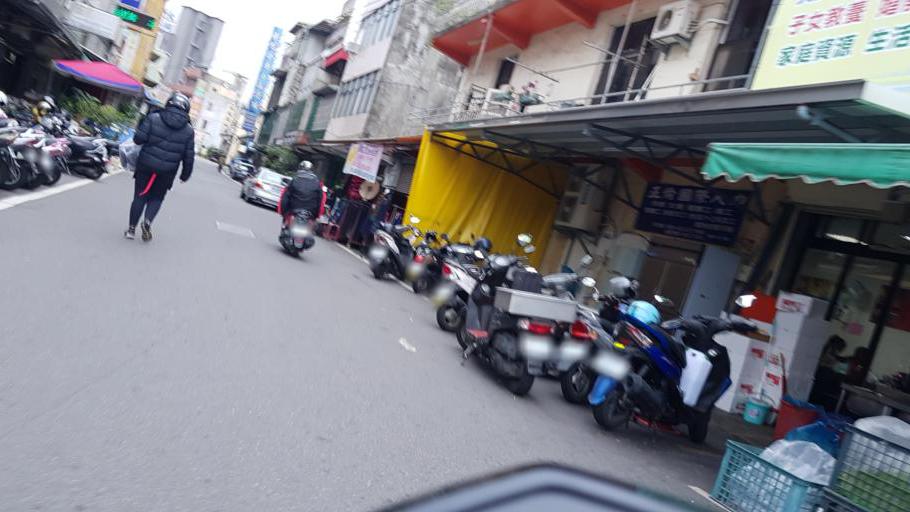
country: TW
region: Taiwan
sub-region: Hsinchu
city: Zhubei
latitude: 24.7389
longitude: 121.0909
